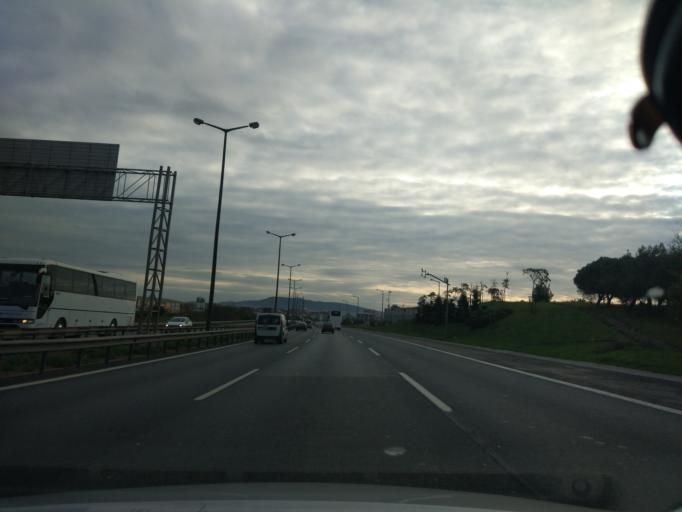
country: TR
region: Istanbul
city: Samandira
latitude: 40.9824
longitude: 29.2067
